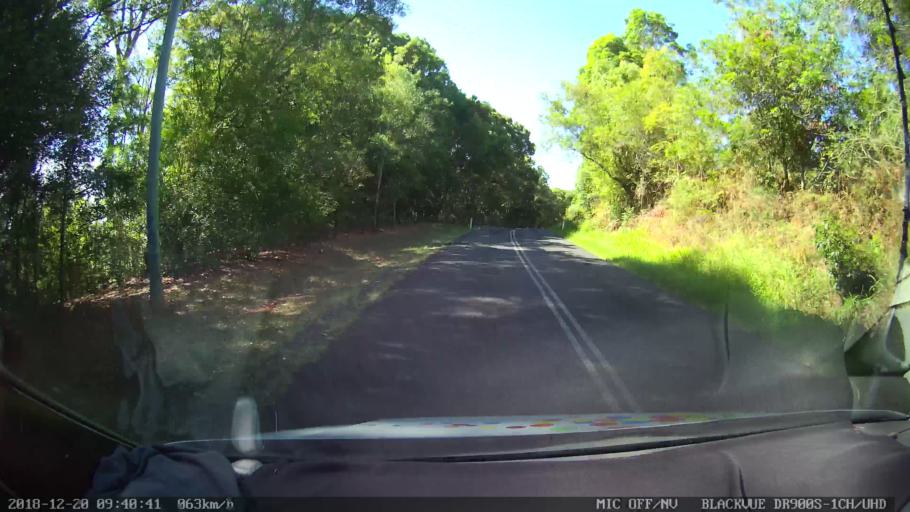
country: AU
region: New South Wales
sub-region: Lismore Municipality
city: Lismore
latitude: -28.7029
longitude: 153.3029
